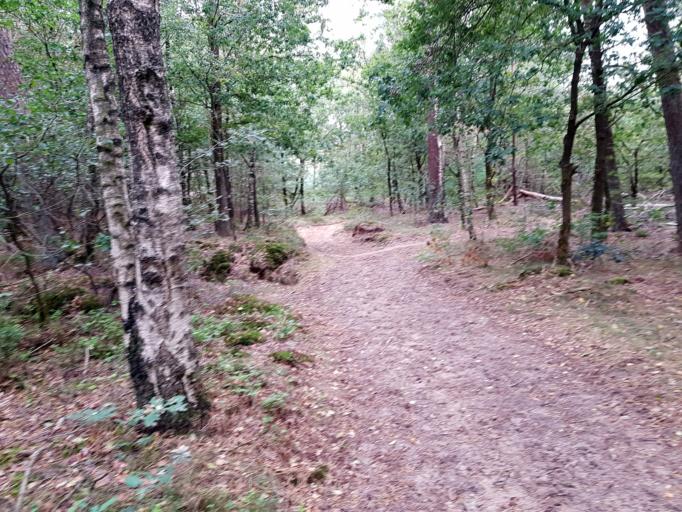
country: NL
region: Utrecht
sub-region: Gemeente Utrechtse Heuvelrug
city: Amerongen
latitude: 52.0164
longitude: 5.4494
